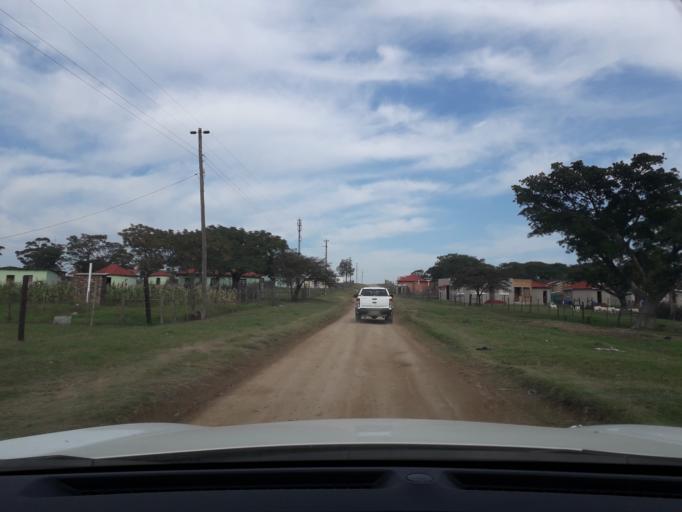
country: ZA
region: Eastern Cape
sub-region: Buffalo City Metropolitan Municipality
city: Bhisho
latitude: -32.9900
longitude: 27.3585
